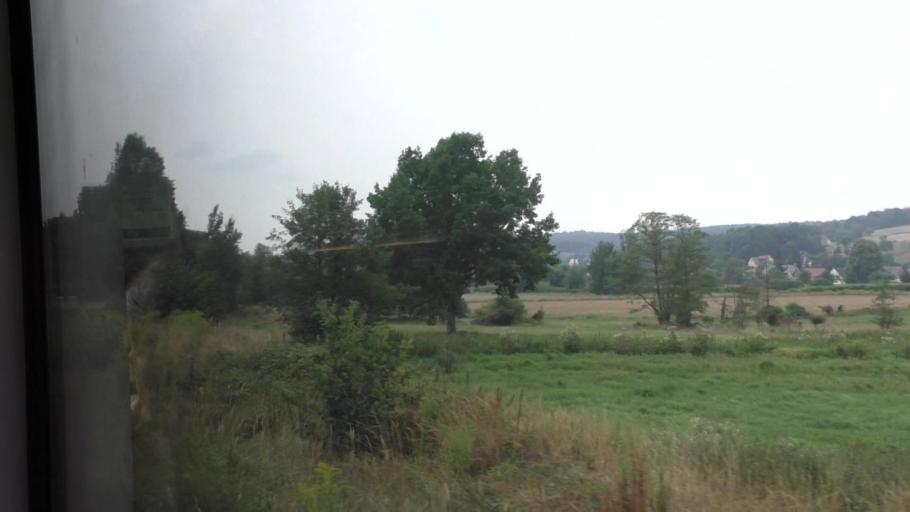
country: DE
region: Saxony
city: Ostritz
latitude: 51.0086
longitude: 14.9382
